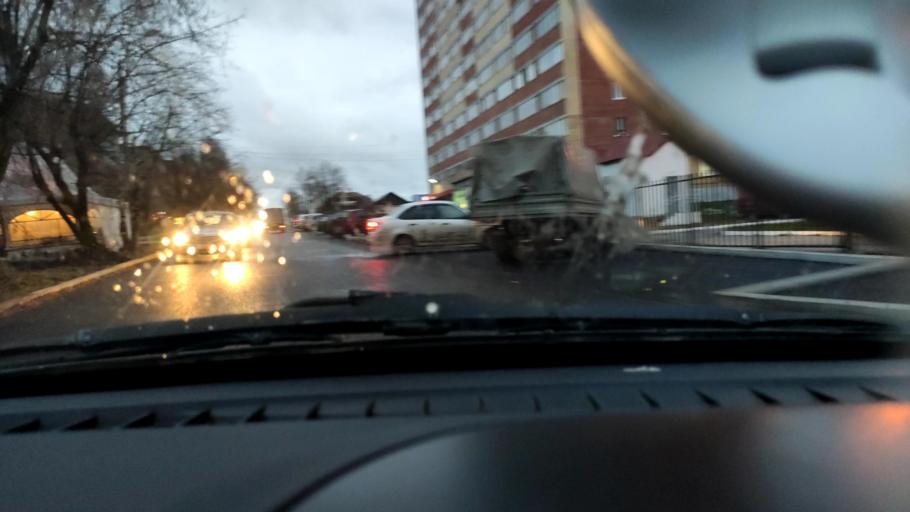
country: RU
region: Perm
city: Kondratovo
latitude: 58.0485
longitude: 56.0871
